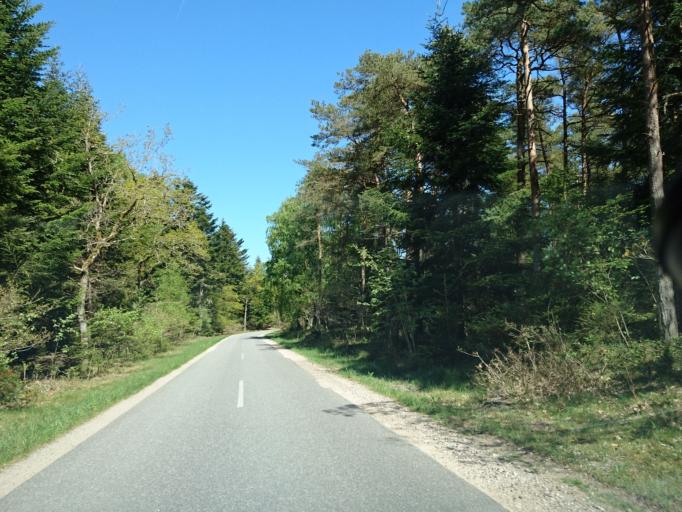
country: DK
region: North Denmark
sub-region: Hjorring Kommune
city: Sindal
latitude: 57.5999
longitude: 10.2330
